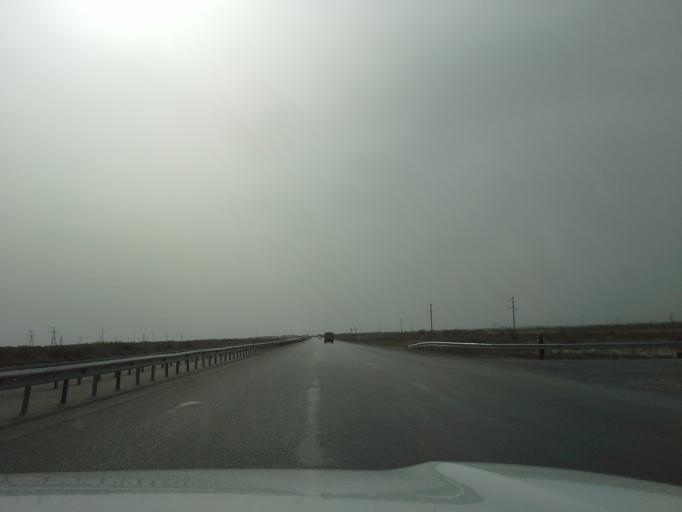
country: TM
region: Ahal
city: Kaka
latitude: 37.4913
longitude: 59.4664
